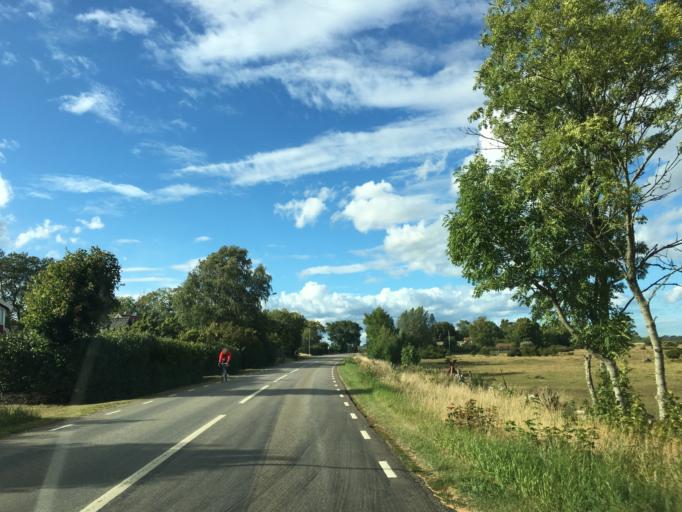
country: SE
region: Kalmar
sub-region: Morbylanga Kommun
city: Moerbylanga
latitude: 56.4433
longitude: 16.4271
